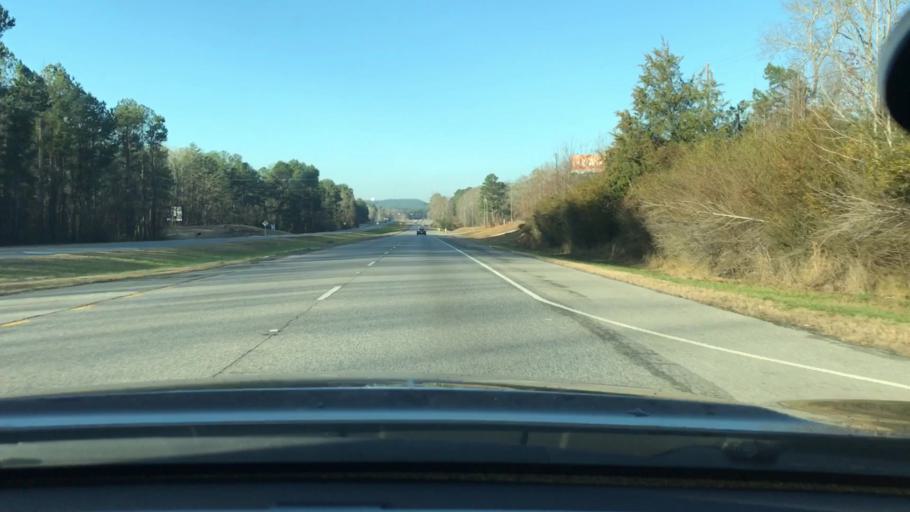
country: US
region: Alabama
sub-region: Shelby County
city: Westover
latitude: 33.3495
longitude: -86.5515
